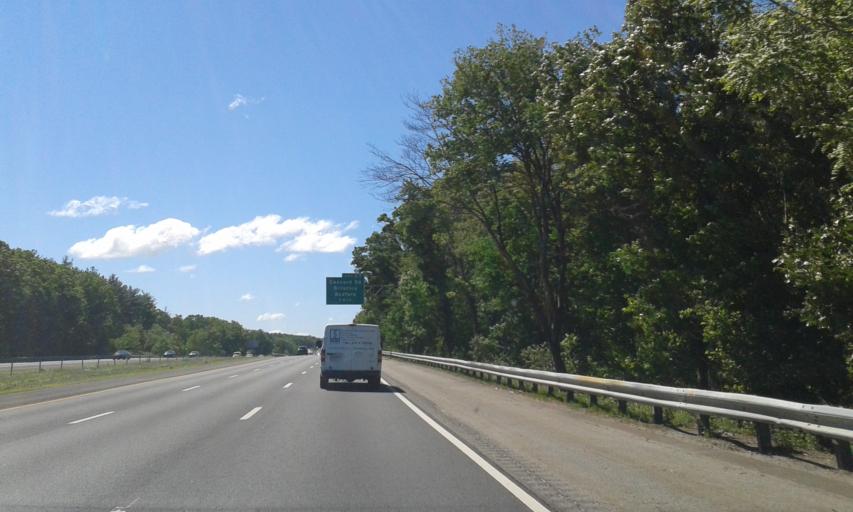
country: US
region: Massachusetts
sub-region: Middlesex County
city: Billerica
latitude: 42.5576
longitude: -71.2955
